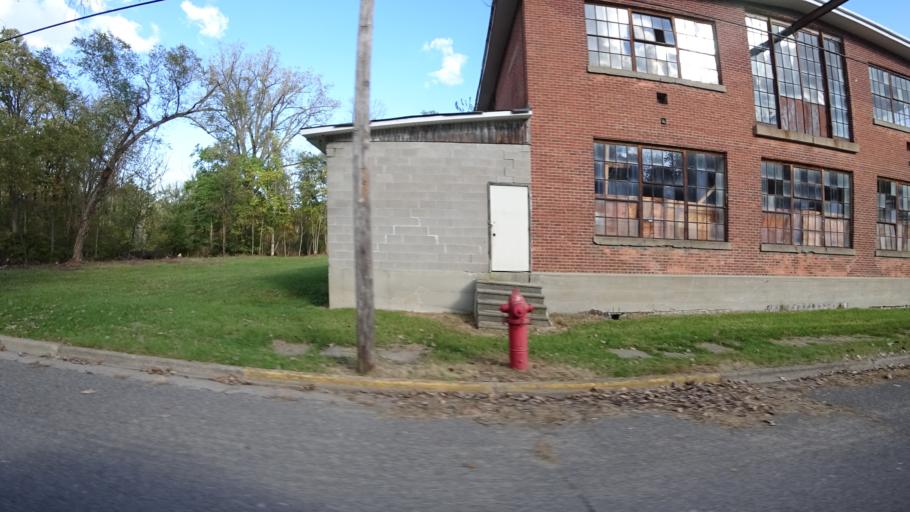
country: US
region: Michigan
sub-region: Saint Joseph County
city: Centreville
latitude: 41.9286
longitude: -85.5283
